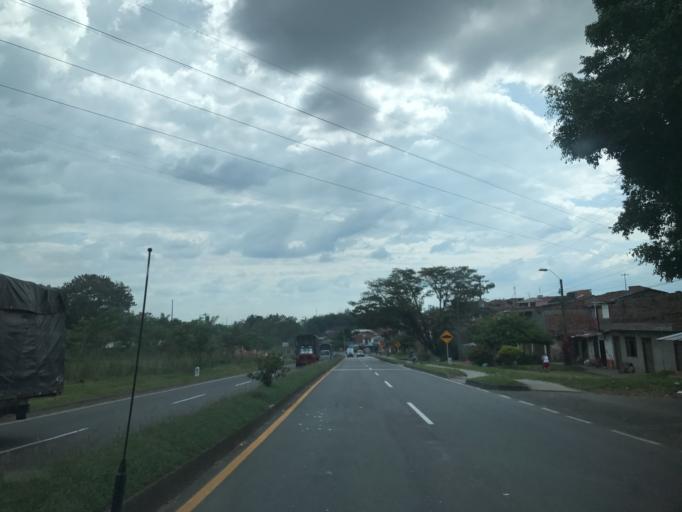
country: CO
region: Valle del Cauca
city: Cartago
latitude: 4.7615
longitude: -75.8983
